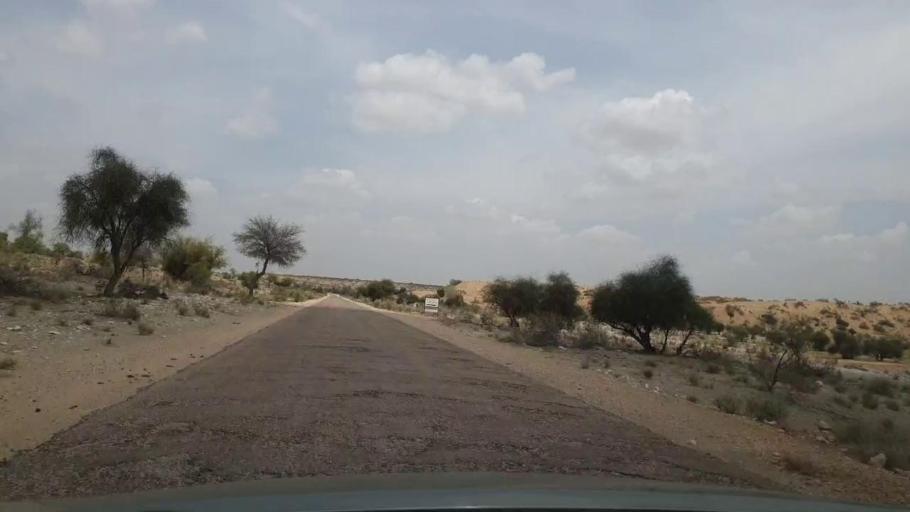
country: PK
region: Sindh
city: Kot Diji
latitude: 27.1747
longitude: 69.1913
